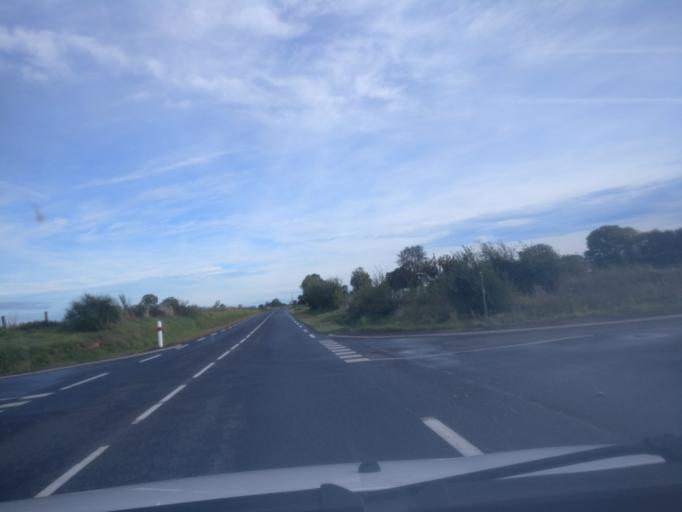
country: FR
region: Lower Normandy
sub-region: Departement de la Manche
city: Sartilly
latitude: 48.7545
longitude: -1.4695
